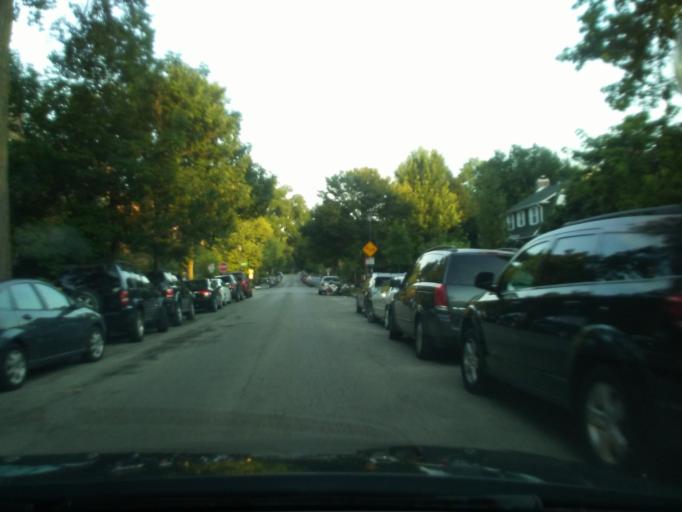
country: US
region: Illinois
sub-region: Cook County
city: Evanston
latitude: 42.0298
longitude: -87.6833
